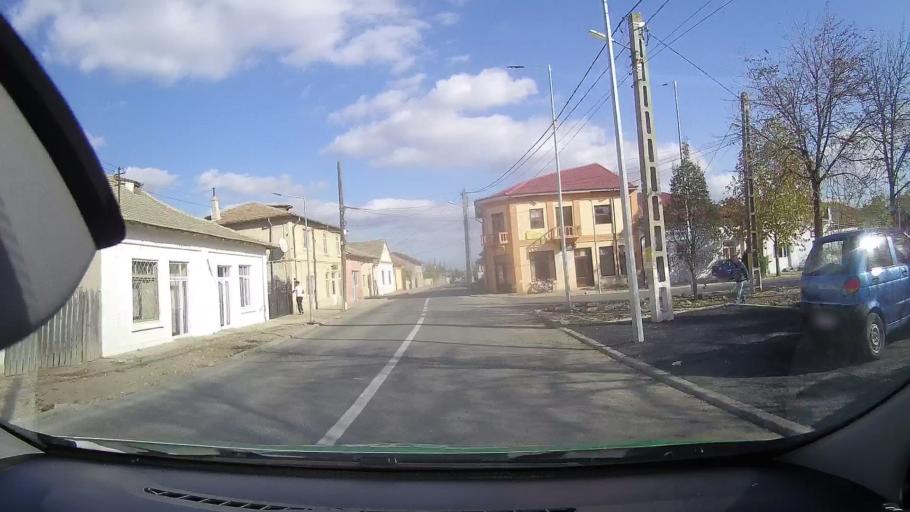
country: RO
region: Constanta
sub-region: Comuna Cogealac
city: Cogealac
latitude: 44.5572
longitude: 28.5655
